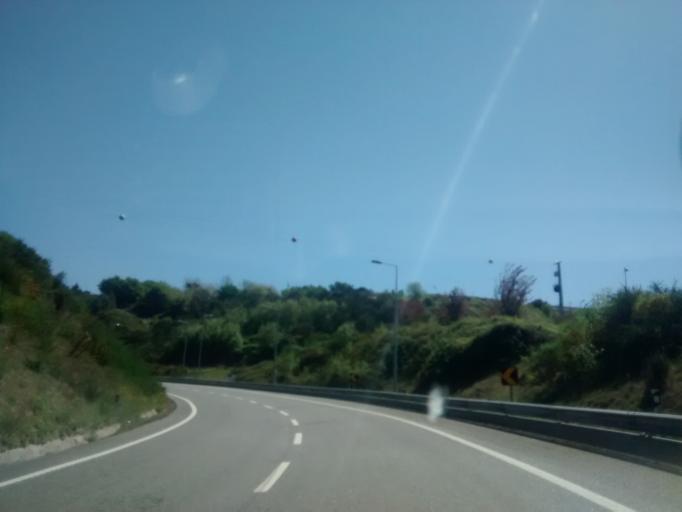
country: PT
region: Braga
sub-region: Guimaraes
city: Selho
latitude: 41.4292
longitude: -8.3382
